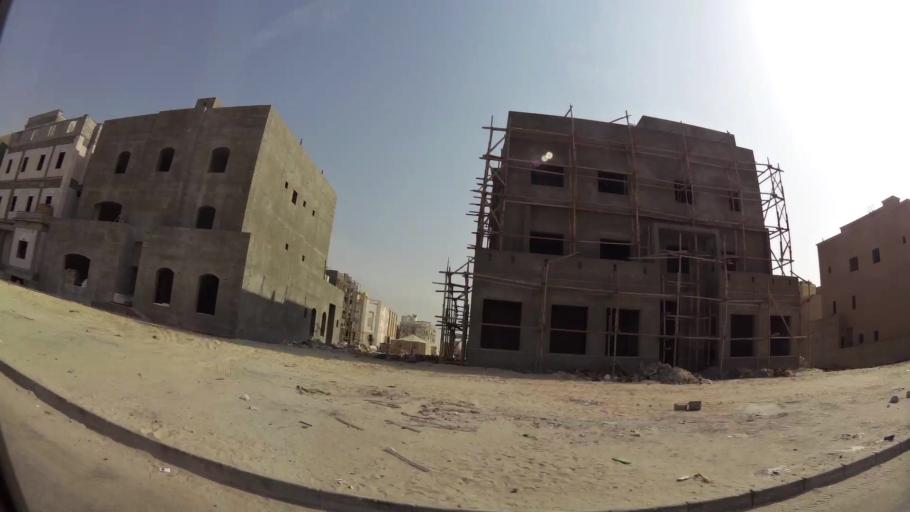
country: KW
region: Muhafazat al Jahra'
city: Al Jahra'
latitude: 29.3494
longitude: 47.7720
